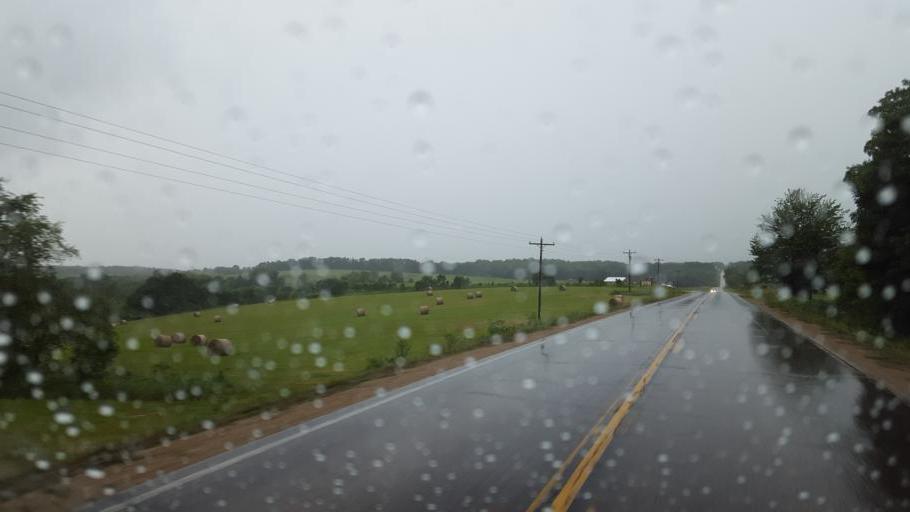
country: US
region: Wisconsin
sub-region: Vernon County
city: Hillsboro
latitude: 43.6236
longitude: -90.4524
